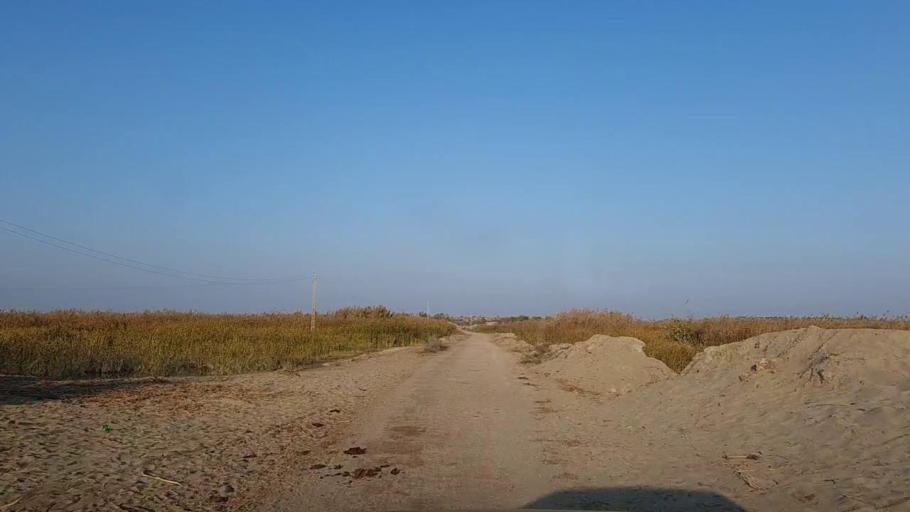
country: PK
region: Sindh
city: Sanghar
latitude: 26.2989
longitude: 68.9898
